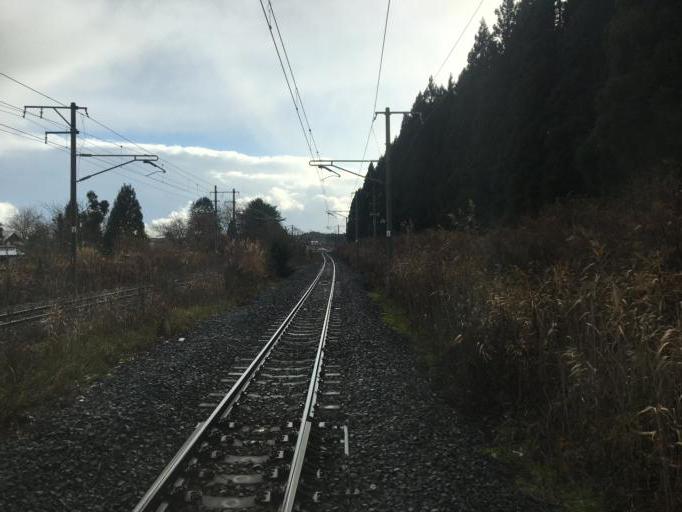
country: JP
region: Aomori
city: Aomori Shi
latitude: 40.9190
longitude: 141.0295
